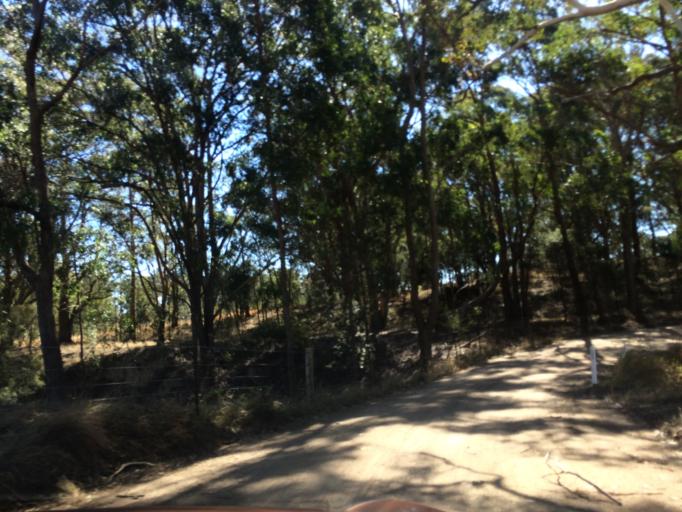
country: AU
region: Queensland
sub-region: Southern Downs
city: Stanthorpe
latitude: -28.6615
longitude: 152.0871
